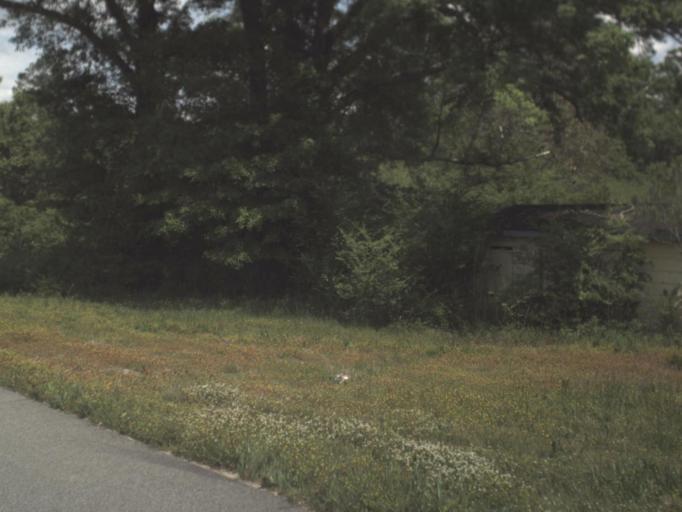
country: US
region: Alabama
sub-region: Escambia County
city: Atmore
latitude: 30.9857
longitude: -87.4917
